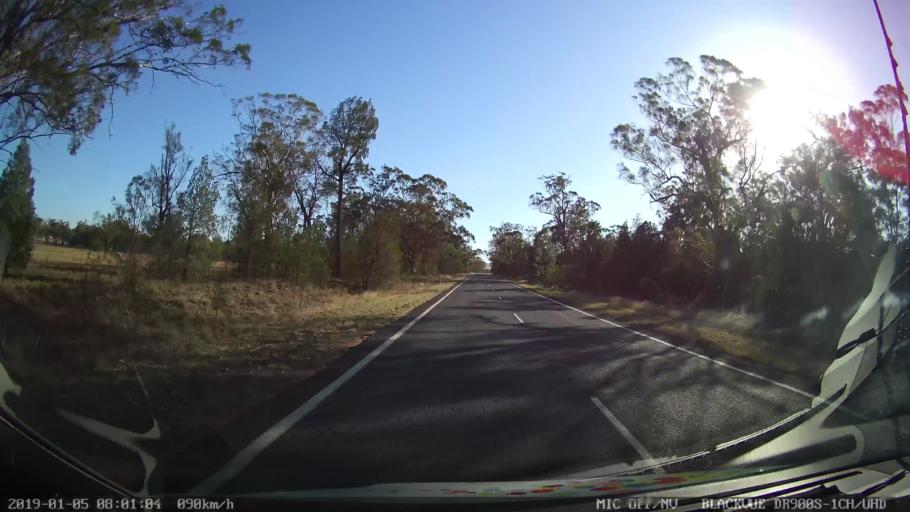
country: AU
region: New South Wales
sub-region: Gilgandra
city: Gilgandra
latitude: -31.6891
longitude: 148.6973
